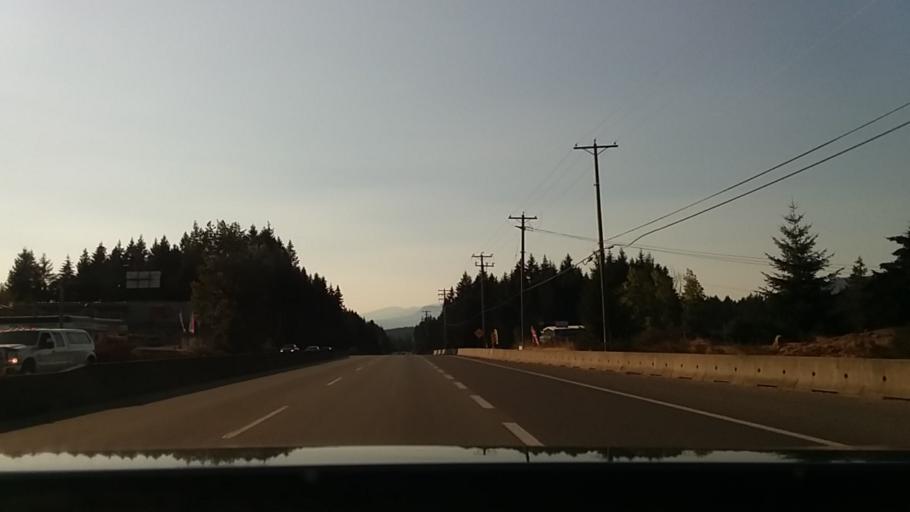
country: CA
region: British Columbia
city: Duncan
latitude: 48.6963
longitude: -123.5919
